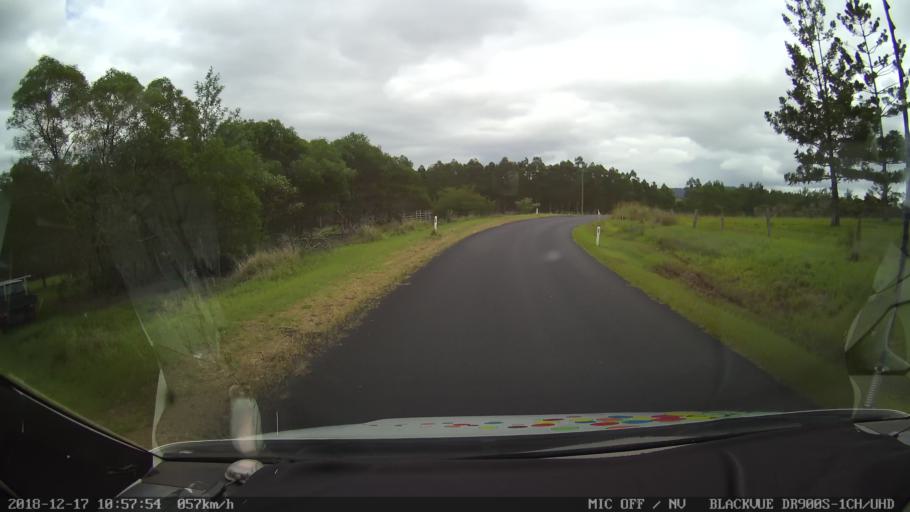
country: AU
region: New South Wales
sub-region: Richmond Valley
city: Casino
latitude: -28.8223
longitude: 152.5999
